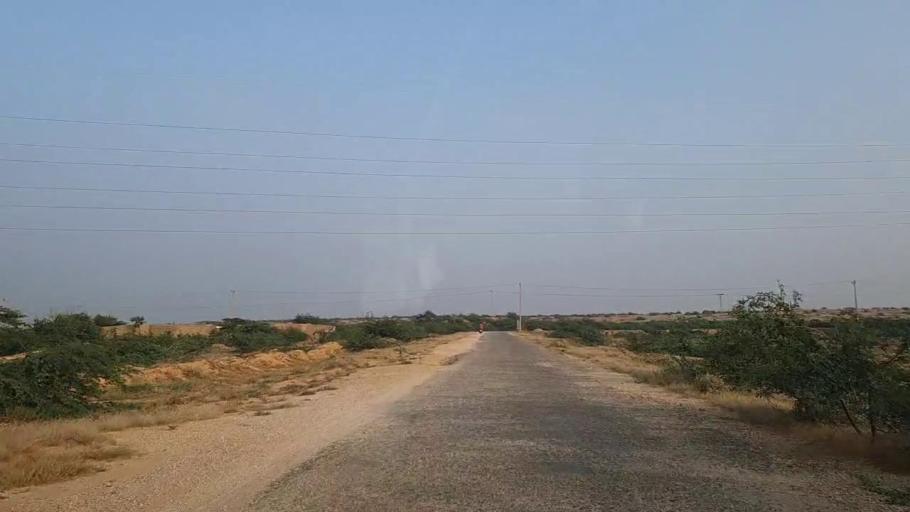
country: PK
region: Sindh
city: Thatta
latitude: 24.6886
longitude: 67.8514
